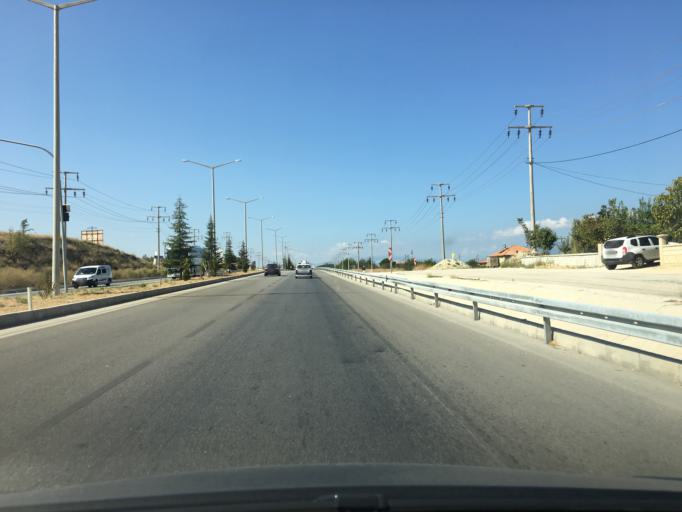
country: TR
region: Burdur
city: Burdur
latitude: 37.7510
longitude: 30.3303
